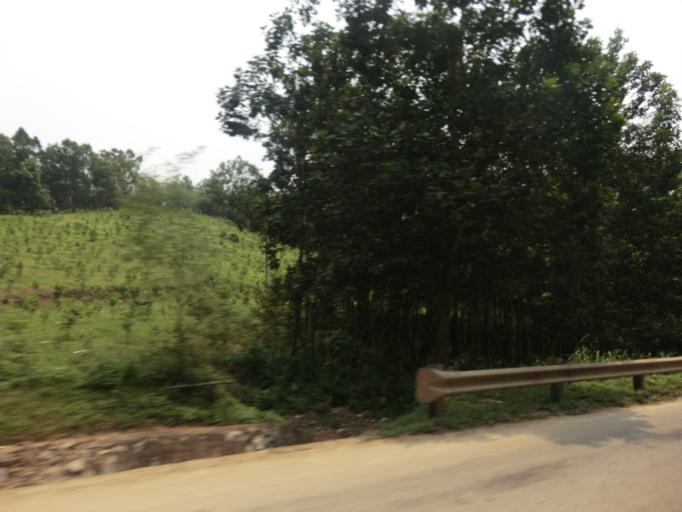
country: VN
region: Thanh Hoa
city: Thi Tran Thuong Xuan
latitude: 19.8589
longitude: 105.4085
